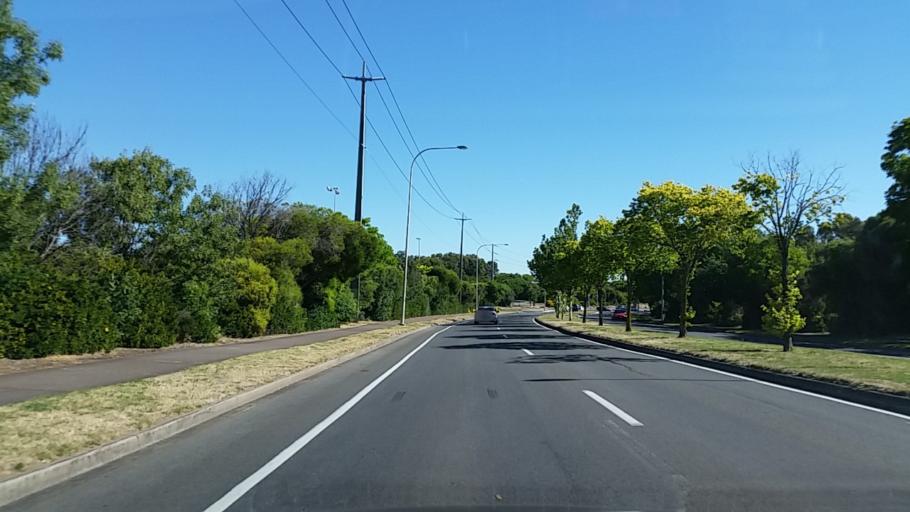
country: AU
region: South Australia
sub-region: Tea Tree Gully
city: Modbury
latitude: -34.8019
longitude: 138.6851
